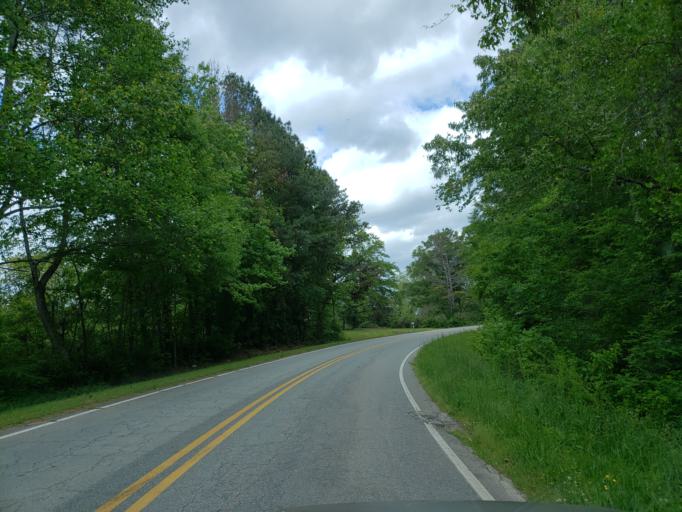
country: US
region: Georgia
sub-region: Haralson County
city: Tallapoosa
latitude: 33.6973
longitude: -85.3448
